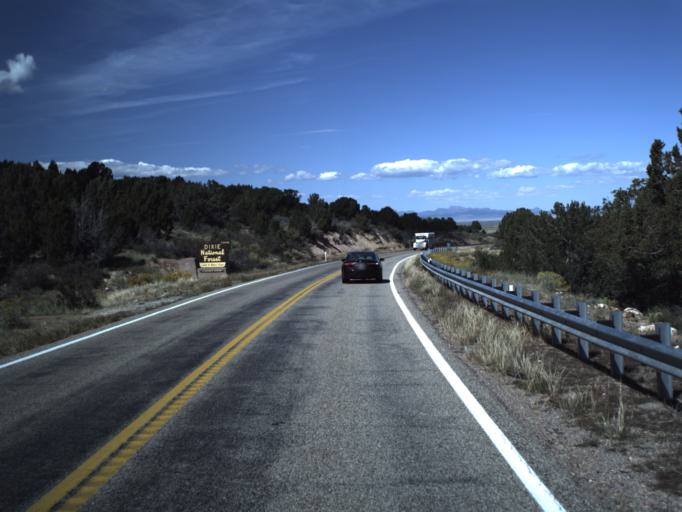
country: US
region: Utah
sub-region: Washington County
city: Enterprise
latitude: 37.5582
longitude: -113.6908
